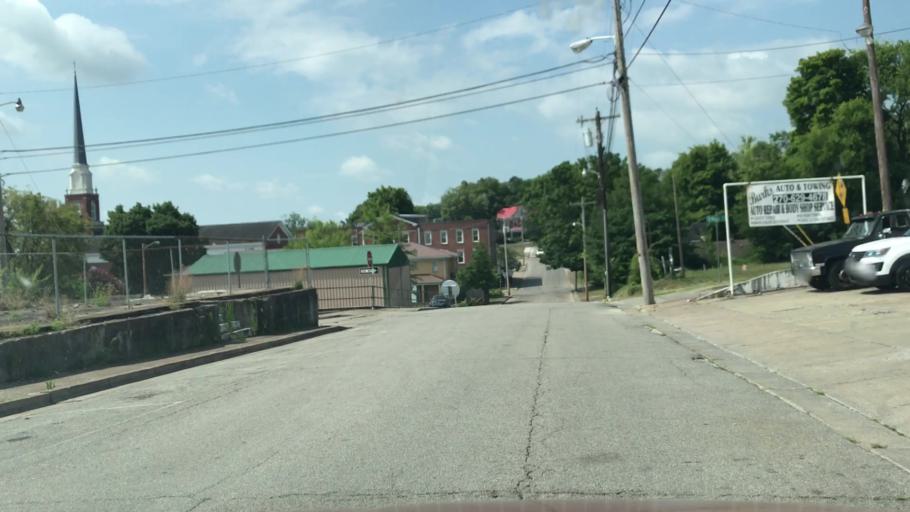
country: US
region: Kentucky
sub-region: Barren County
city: Glasgow
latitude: 36.9949
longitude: -85.9139
